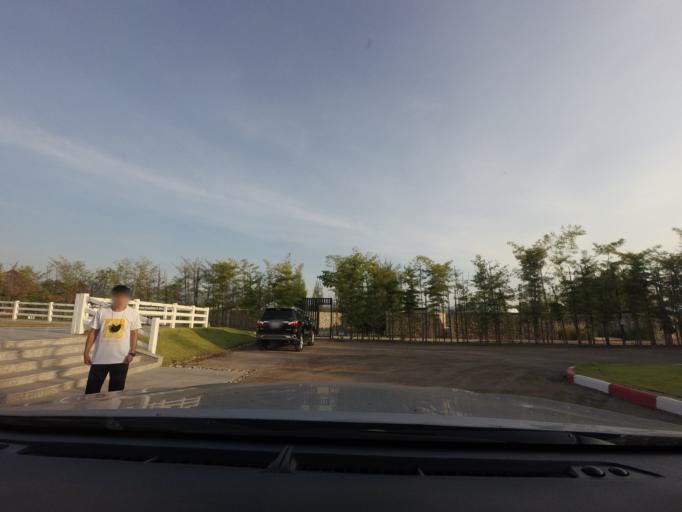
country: TH
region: Chiang Mai
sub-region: Amphoe Chiang Dao
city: Chiang Dao
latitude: 19.3340
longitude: 98.9622
